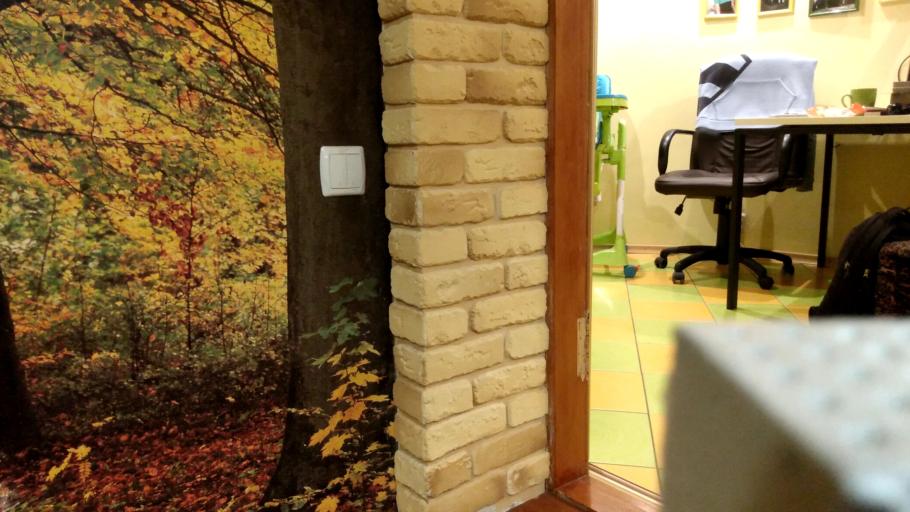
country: RU
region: Republic of Karelia
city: Pudozh
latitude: 61.7950
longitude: 37.6736
